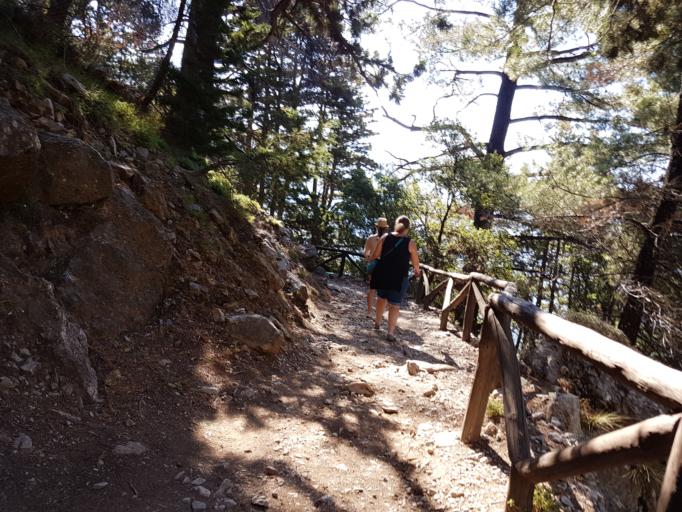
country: GR
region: Crete
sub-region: Nomos Chanias
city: Perivolia
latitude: 35.3091
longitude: 23.9234
